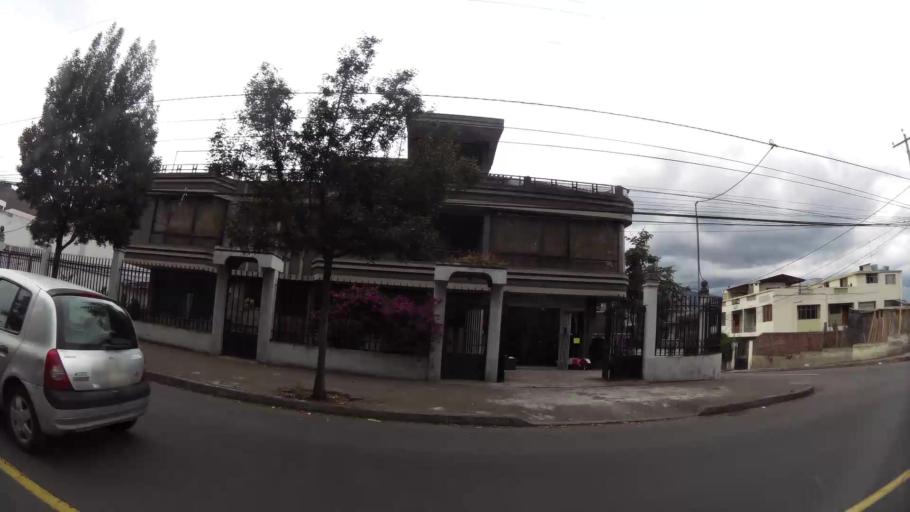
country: EC
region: Tungurahua
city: Ambato
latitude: -1.2517
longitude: -78.6373
